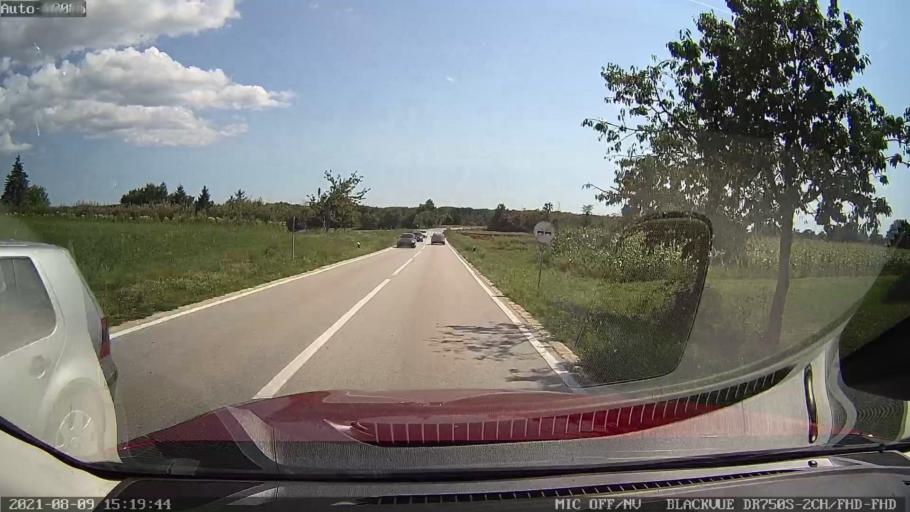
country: HR
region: Istarska
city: Pazin
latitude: 45.2122
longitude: 13.9018
